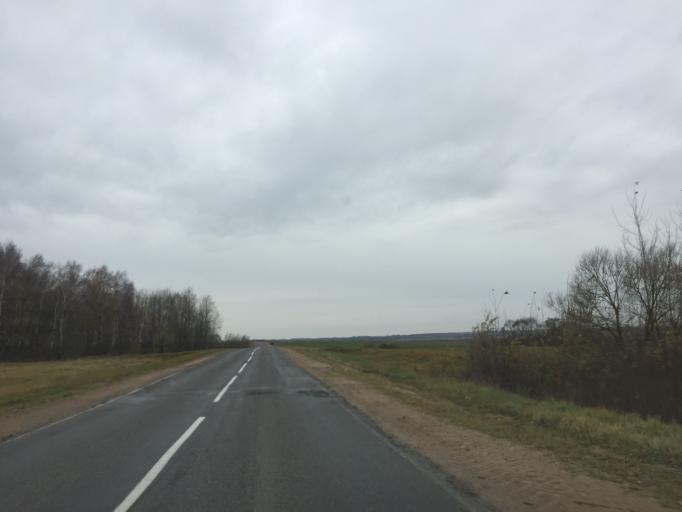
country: BY
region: Mogilev
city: Drybin
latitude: 54.1439
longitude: 31.1191
